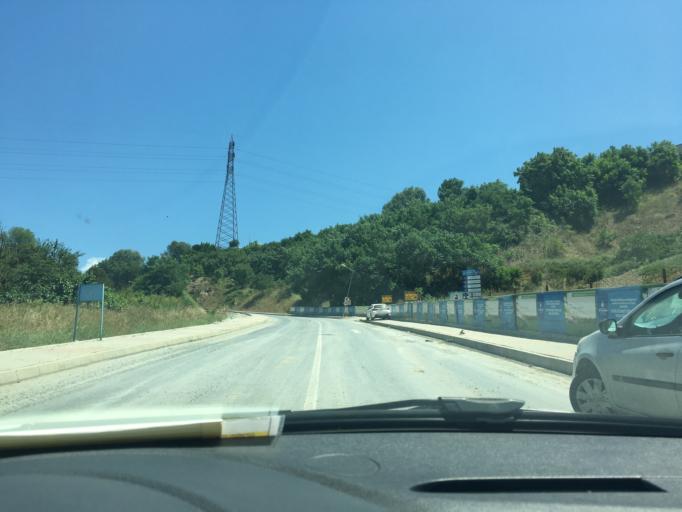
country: TR
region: Istanbul
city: Sisli
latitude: 41.0891
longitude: 28.9556
